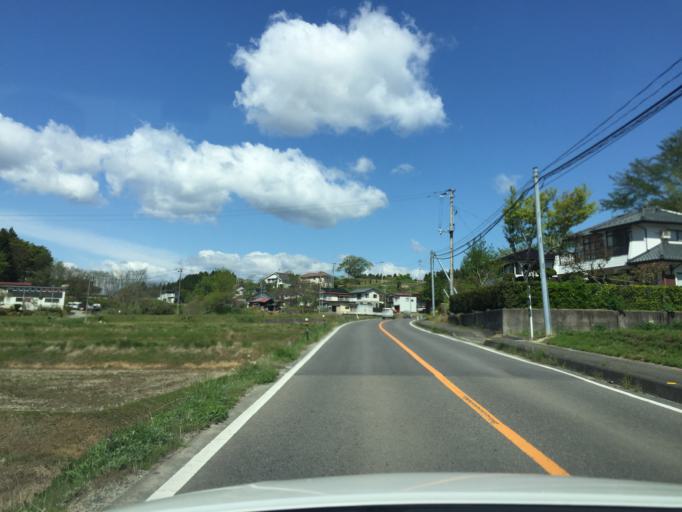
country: JP
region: Fukushima
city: Nihommatsu
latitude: 37.5719
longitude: 140.4726
